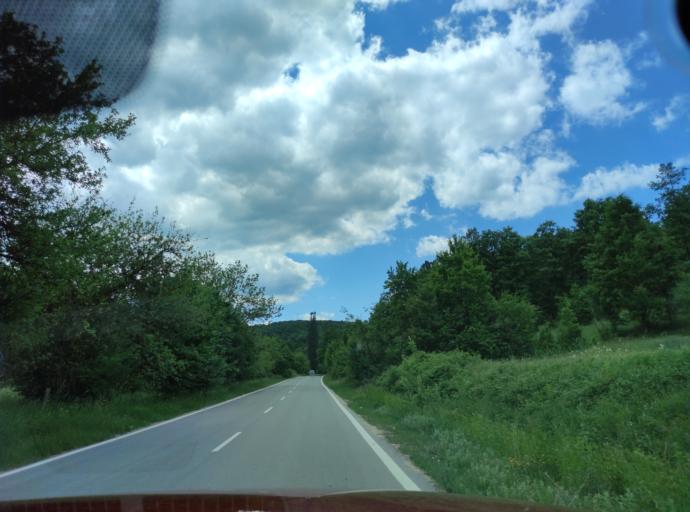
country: BG
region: Montana
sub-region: Obshtina Chiprovtsi
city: Chiprovtsi
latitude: 43.4562
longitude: 22.9003
